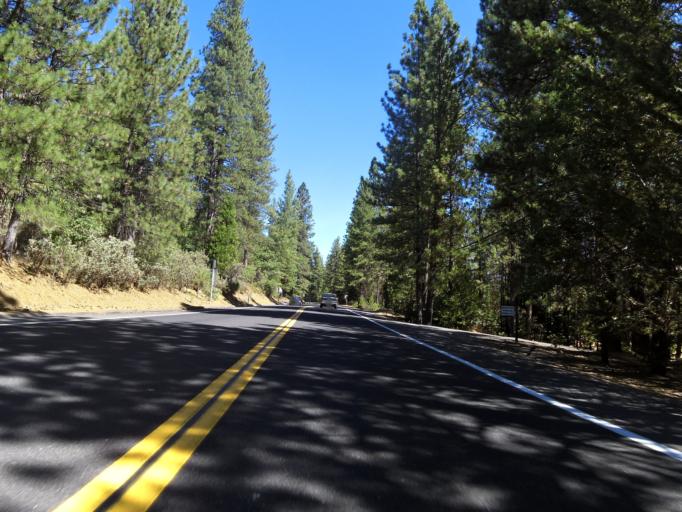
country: US
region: California
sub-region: Calaveras County
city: Arnold
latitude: 38.2069
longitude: -120.3688
